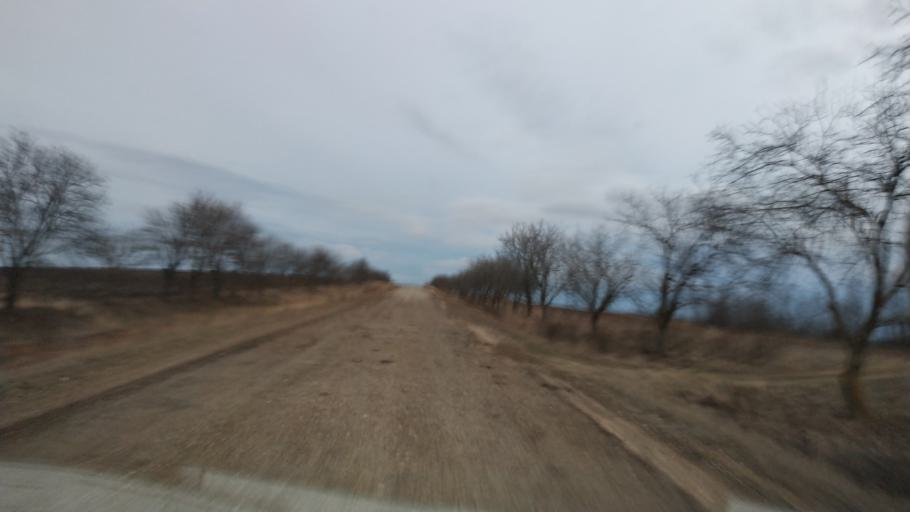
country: MD
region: Causeni
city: Causeni
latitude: 46.5774
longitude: 29.3903
